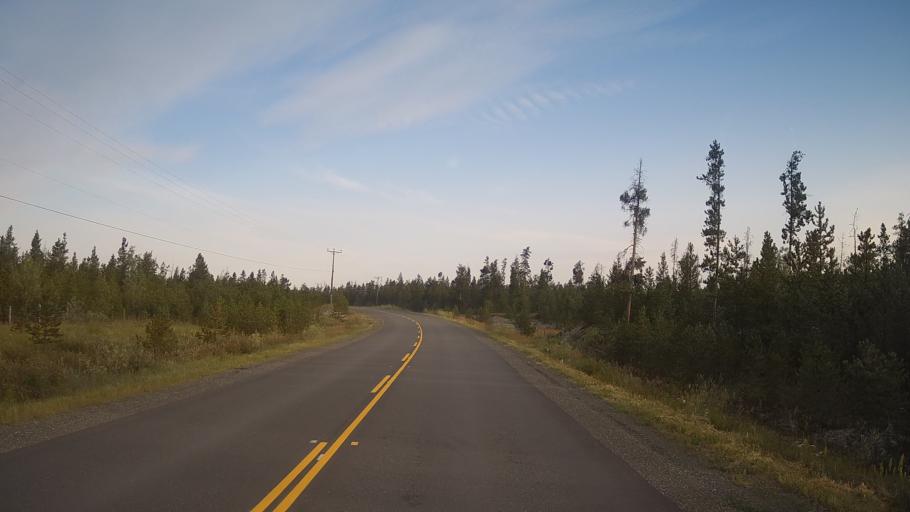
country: CA
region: British Columbia
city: Hanceville
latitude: 52.1359
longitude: -123.7021
